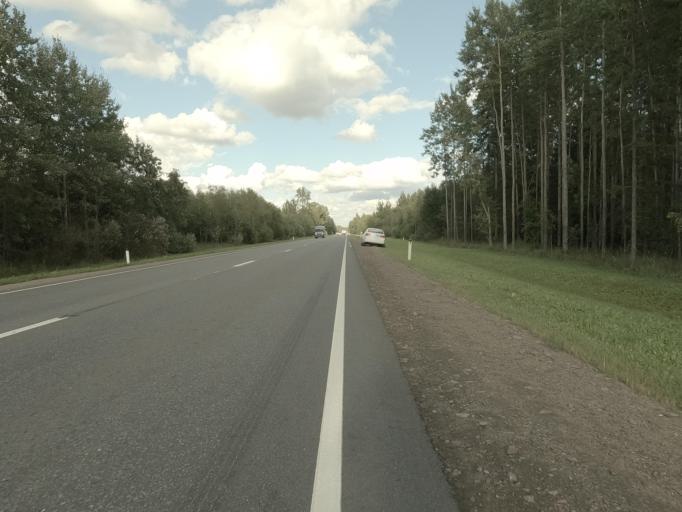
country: RU
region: Leningrad
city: Nikol'skoye
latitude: 59.6711
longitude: 30.9045
